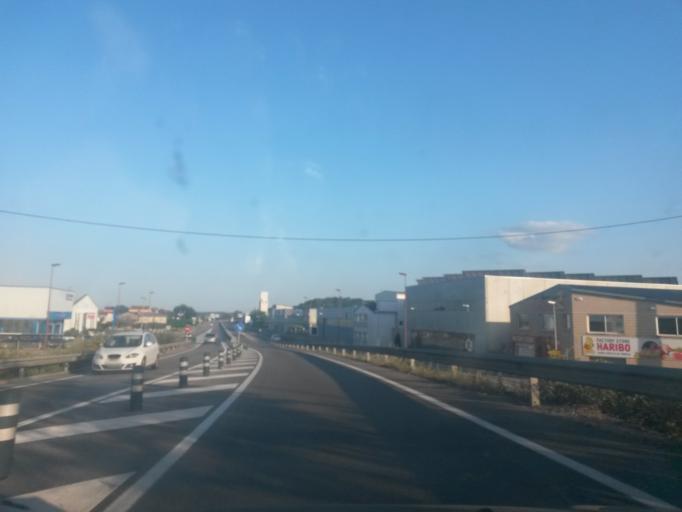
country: ES
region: Catalonia
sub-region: Provincia de Girona
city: Cornella del Terri
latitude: 42.0965
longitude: 2.7986
